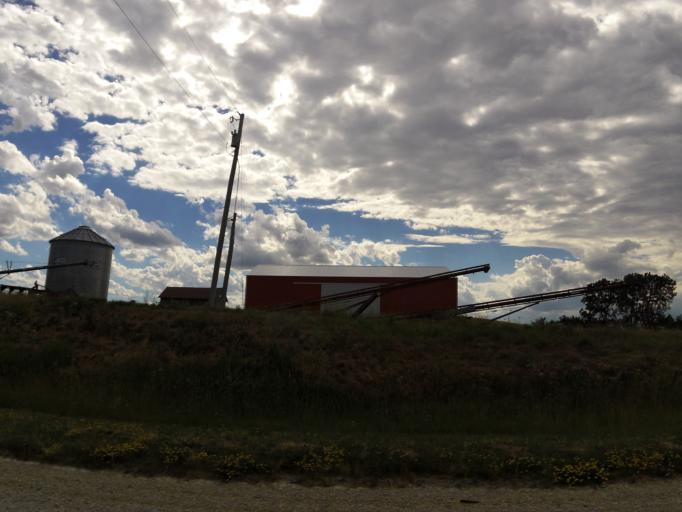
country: US
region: Illinois
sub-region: Hancock County
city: Nauvoo
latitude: 40.7095
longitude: -91.5650
